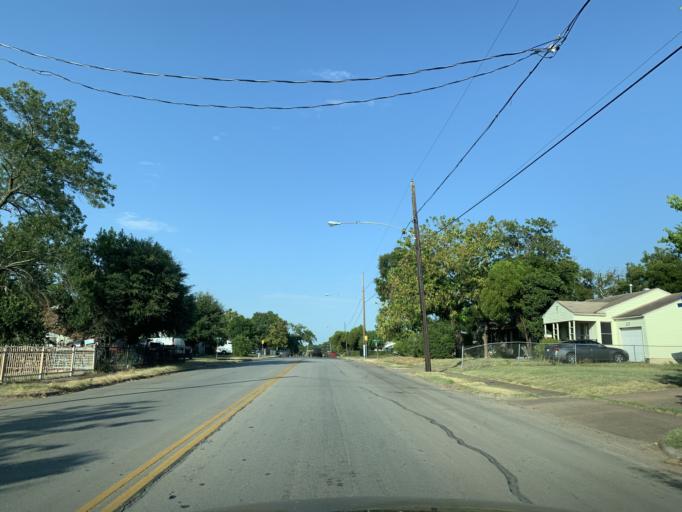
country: US
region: Texas
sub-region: Dallas County
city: Dallas
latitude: 32.7099
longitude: -96.7879
